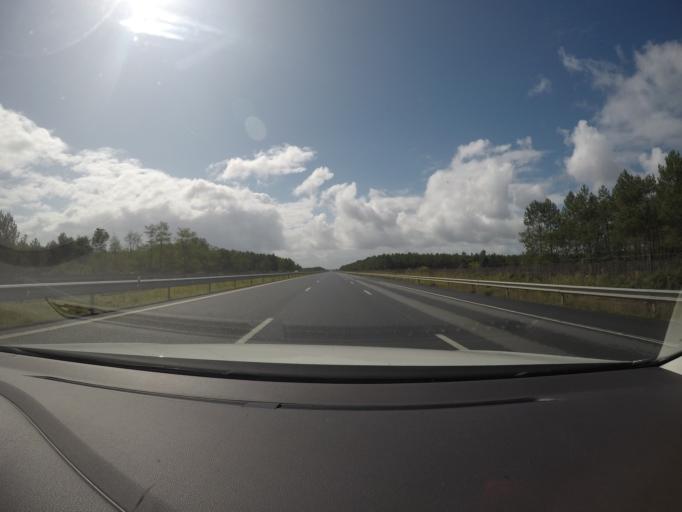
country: FR
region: Aquitaine
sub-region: Departement des Landes
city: Magescq
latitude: 43.8198
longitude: -1.1908
